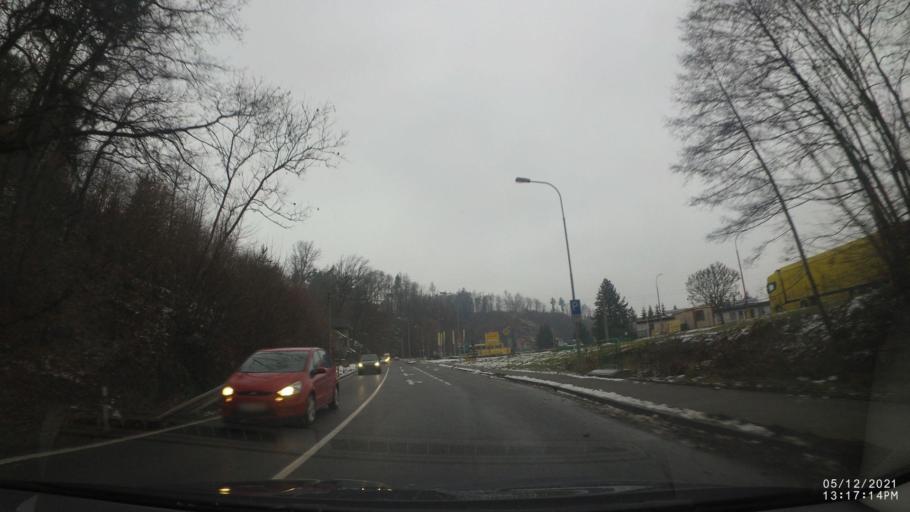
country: CZ
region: Kralovehradecky
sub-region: Okres Nachod
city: Nachod
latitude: 50.4271
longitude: 16.1907
